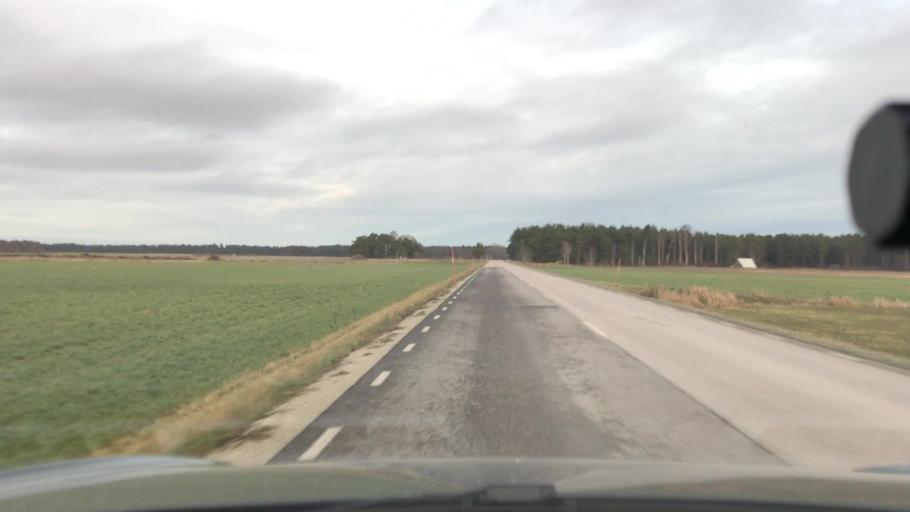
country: SE
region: Gotland
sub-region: Gotland
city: Slite
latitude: 57.7143
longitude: 18.5479
